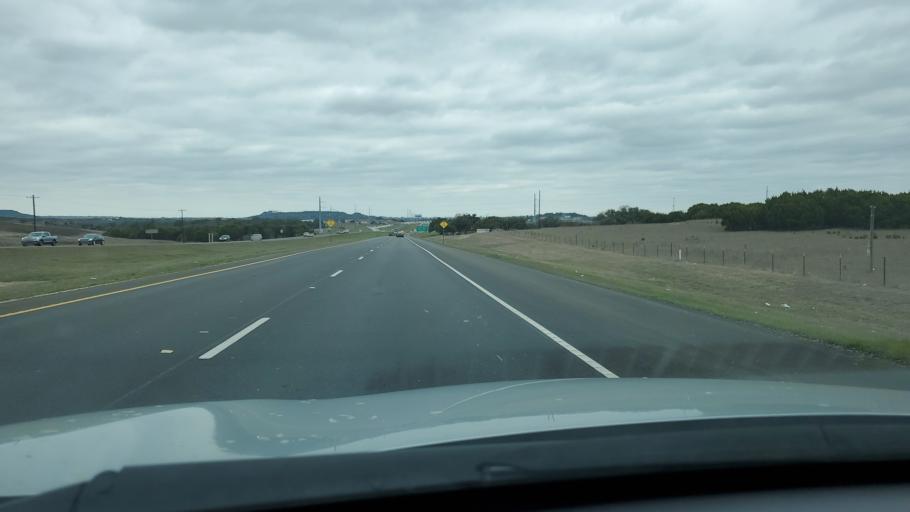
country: US
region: Texas
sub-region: Bell County
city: Killeen
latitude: 31.0470
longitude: -97.7613
